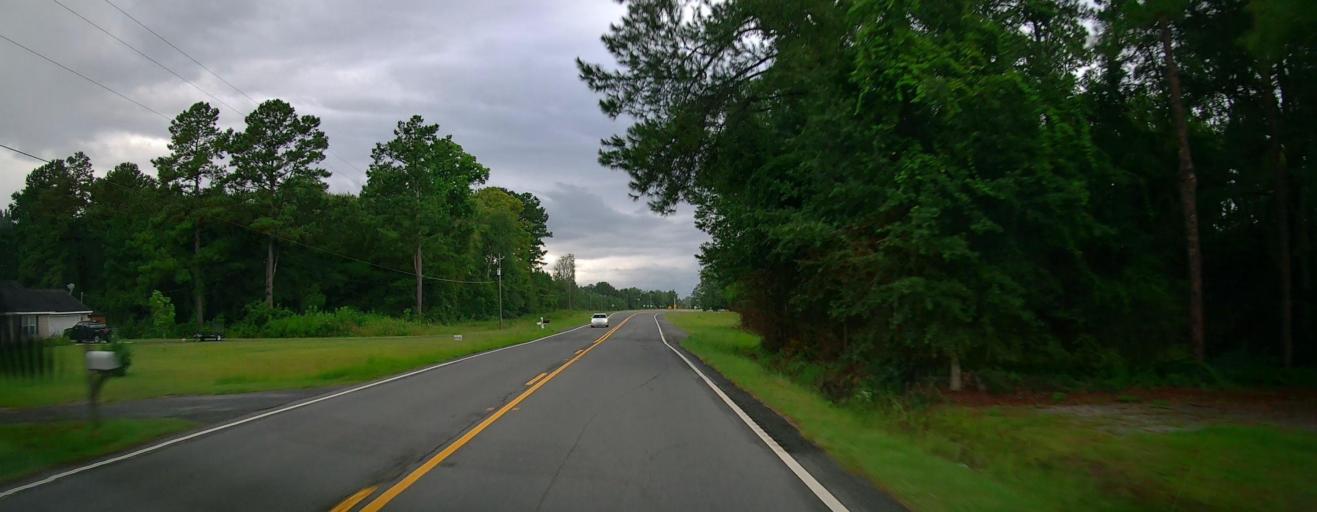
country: US
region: Georgia
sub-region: Ware County
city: Deenwood
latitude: 31.2876
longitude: -82.4413
